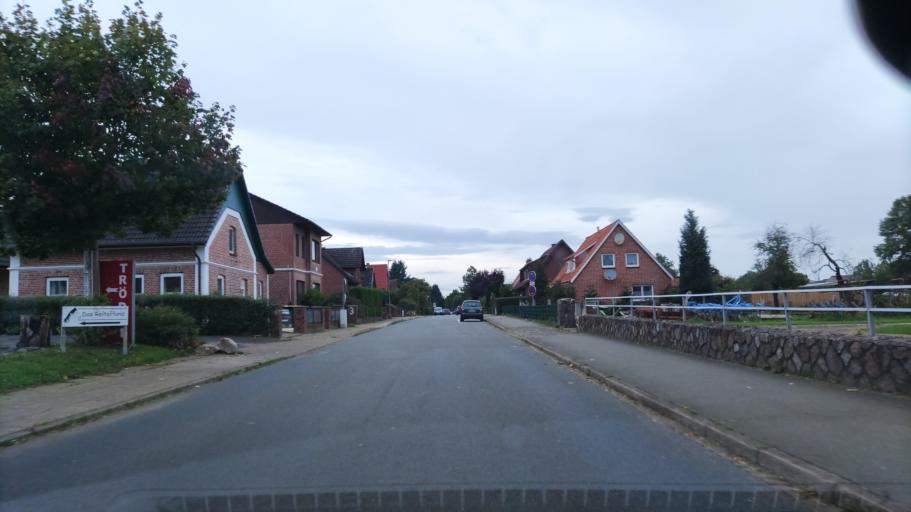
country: DE
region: Schleswig-Holstein
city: Grande
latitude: 53.5805
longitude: 10.3861
